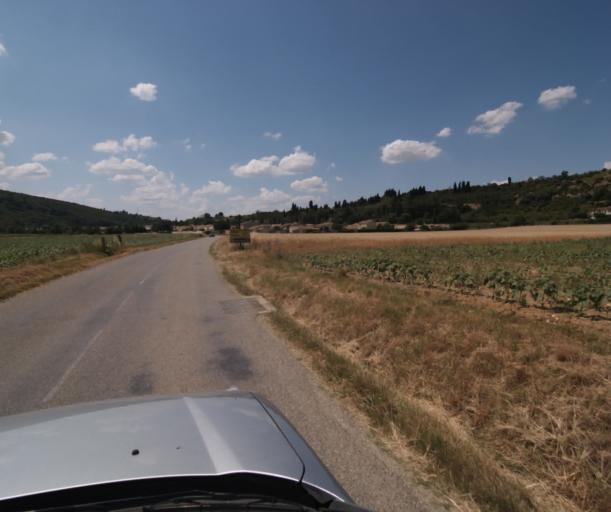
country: FR
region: Languedoc-Roussillon
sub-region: Departement de l'Aude
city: Limoux
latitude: 43.0471
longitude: 2.2335
